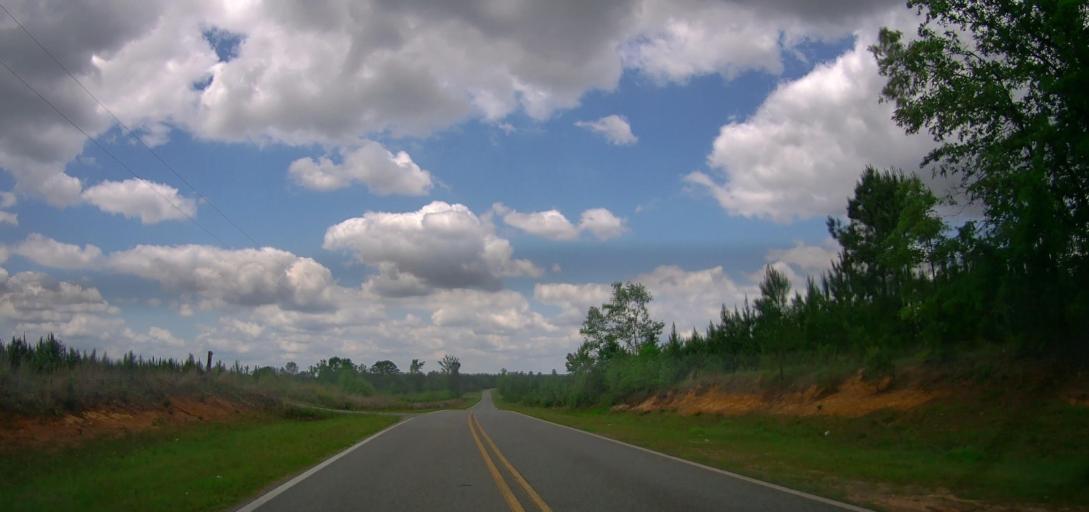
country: US
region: Georgia
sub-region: Laurens County
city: East Dublin
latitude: 32.6051
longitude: -82.8037
